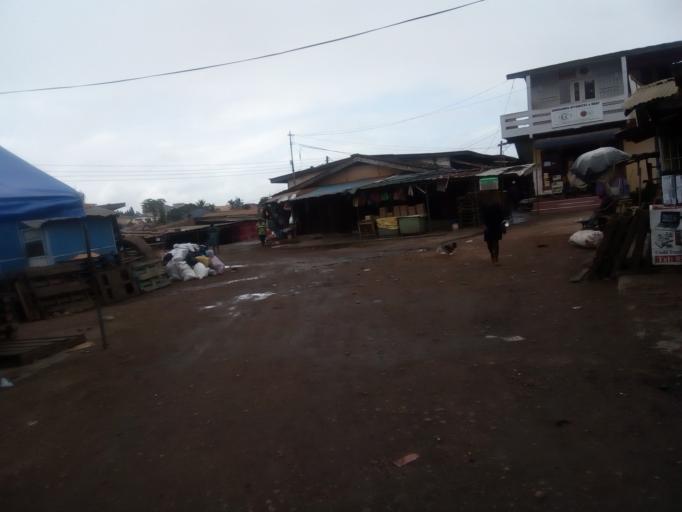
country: GH
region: Greater Accra
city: Dome
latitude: 5.6092
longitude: -0.2561
